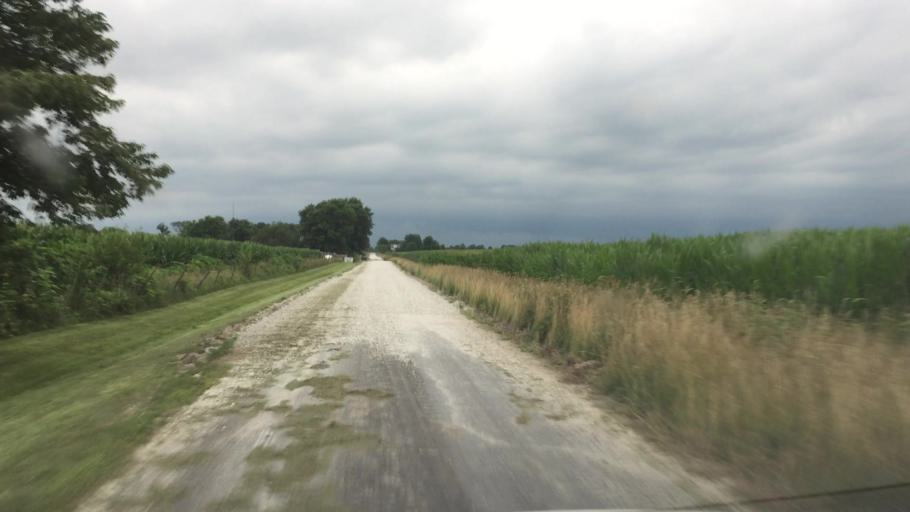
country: US
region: Illinois
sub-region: Adams County
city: Camp Point
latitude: 40.2155
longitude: -90.9606
